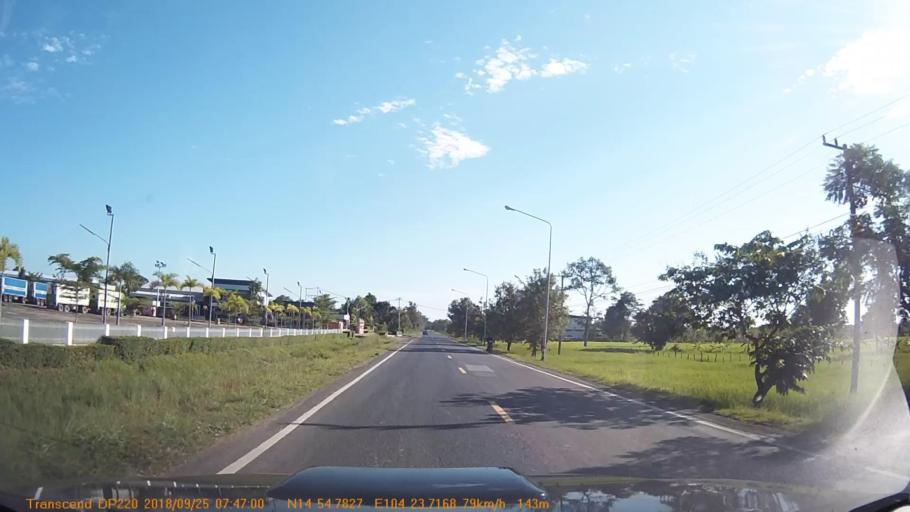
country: TH
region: Sisaket
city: Phayu
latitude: 14.9131
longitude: 104.3953
